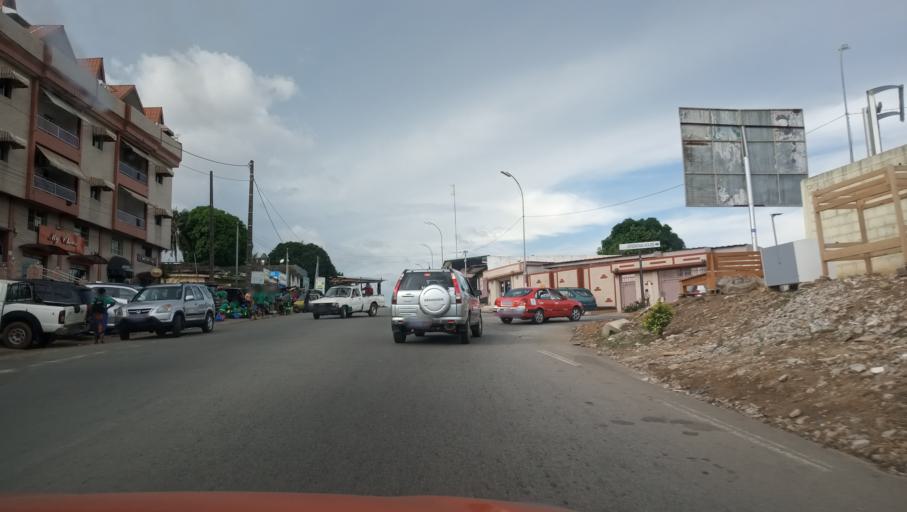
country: CI
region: Lagunes
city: Abidjan
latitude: 5.3503
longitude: -3.9817
